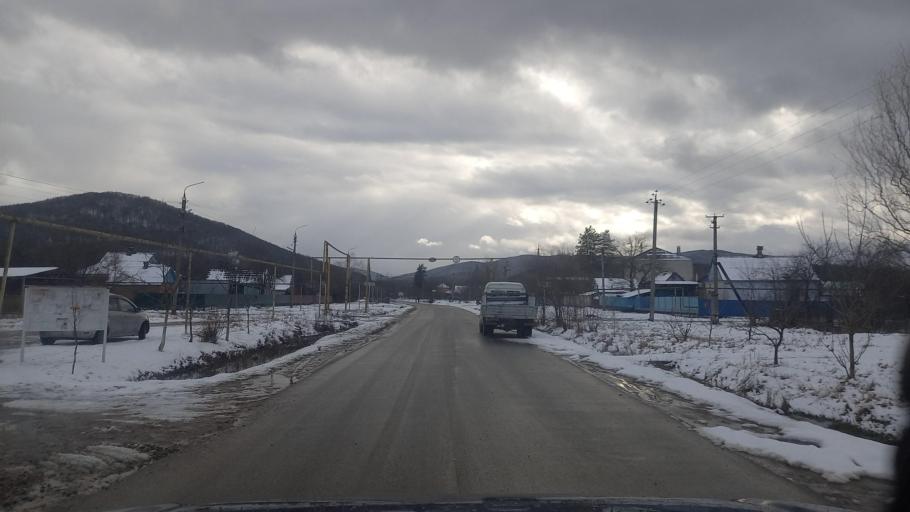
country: RU
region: Krasnodarskiy
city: Smolenskaya
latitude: 44.7152
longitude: 38.8248
